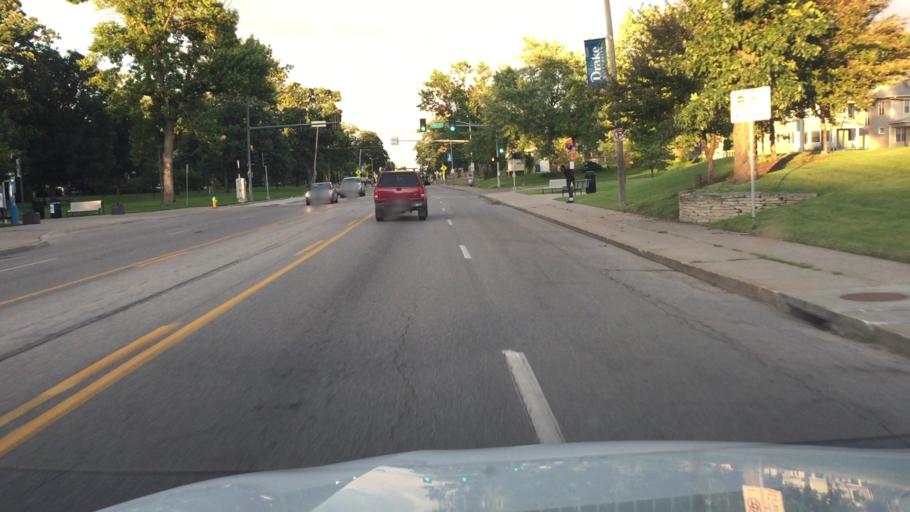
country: US
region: Iowa
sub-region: Polk County
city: Des Moines
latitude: 41.6004
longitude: -93.6554
